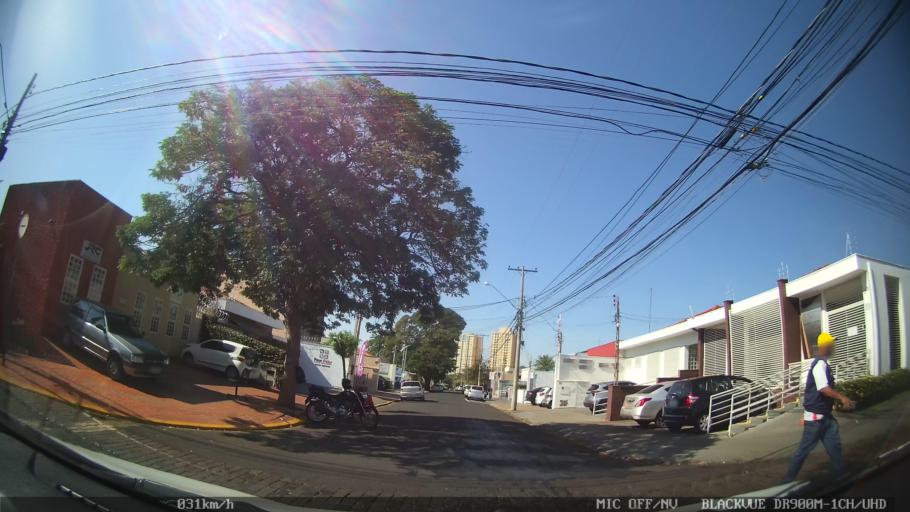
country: BR
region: Sao Paulo
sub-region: Ribeirao Preto
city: Ribeirao Preto
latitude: -21.1905
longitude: -47.8055
